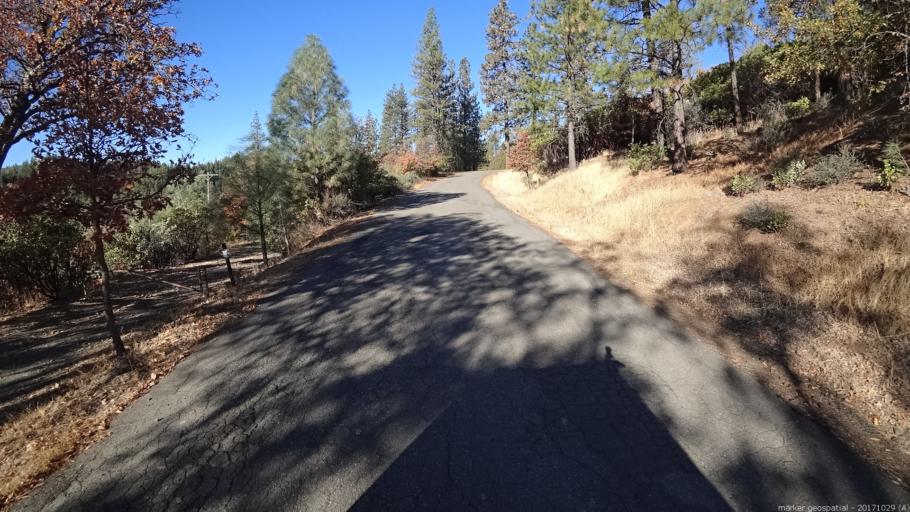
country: US
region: California
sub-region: Trinity County
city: Hayfork
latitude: 40.3628
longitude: -122.9599
